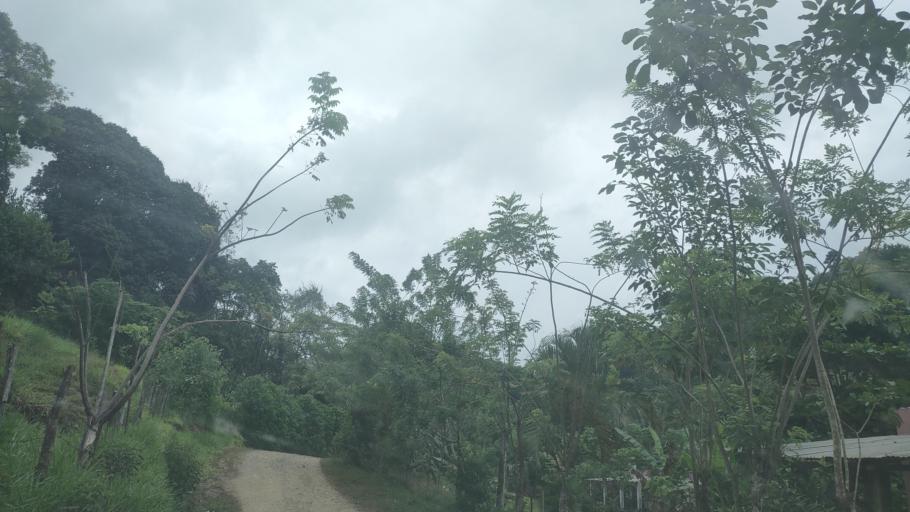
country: MX
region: Tabasco
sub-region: Huimanguillo
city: Francisco Rueda
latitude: 17.4428
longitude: -94.0262
